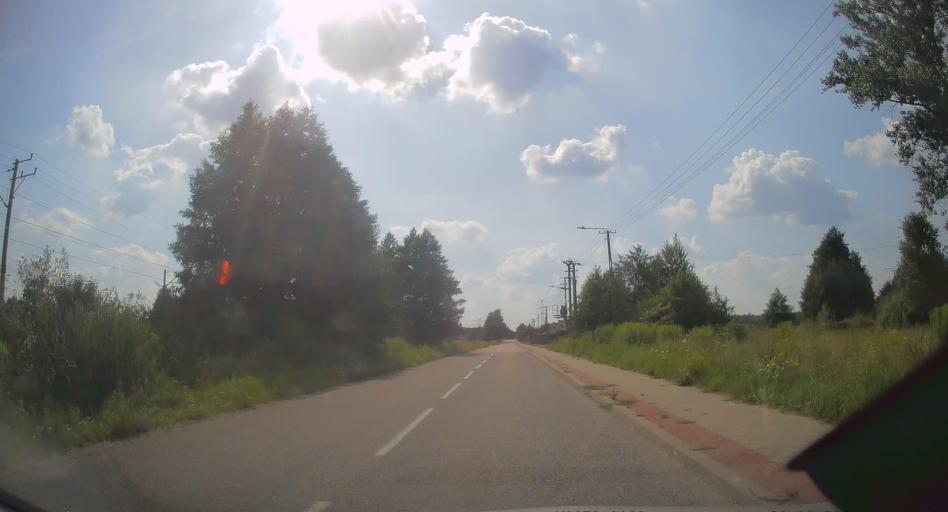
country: PL
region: Swietokrzyskie
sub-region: Powiat jedrzejowski
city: Malogoszcz
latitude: 50.8667
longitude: 20.3172
